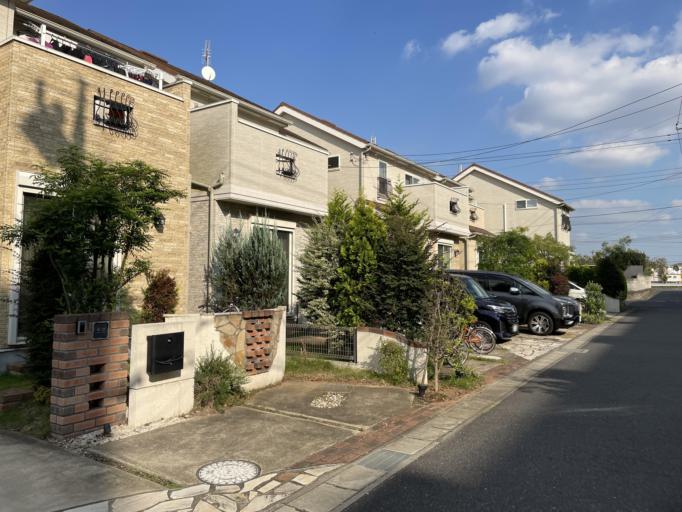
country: JP
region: Chiba
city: Nagareyama
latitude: 35.8301
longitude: 139.9062
